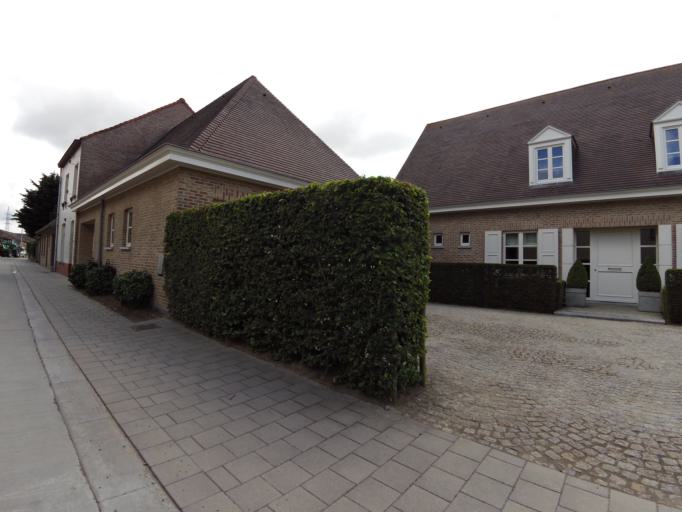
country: BE
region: Flanders
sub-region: Provincie West-Vlaanderen
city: Gistel
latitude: 51.1546
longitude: 2.9515
